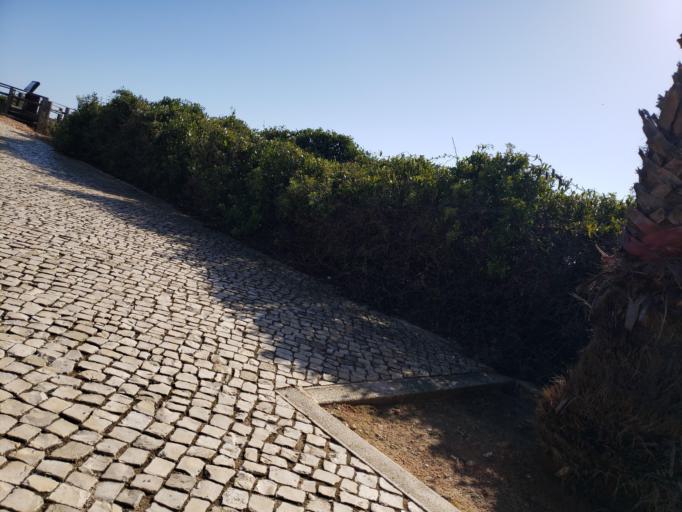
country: PT
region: Faro
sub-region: Lagoa
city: Carvoeiro
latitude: 37.0945
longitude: -8.4682
